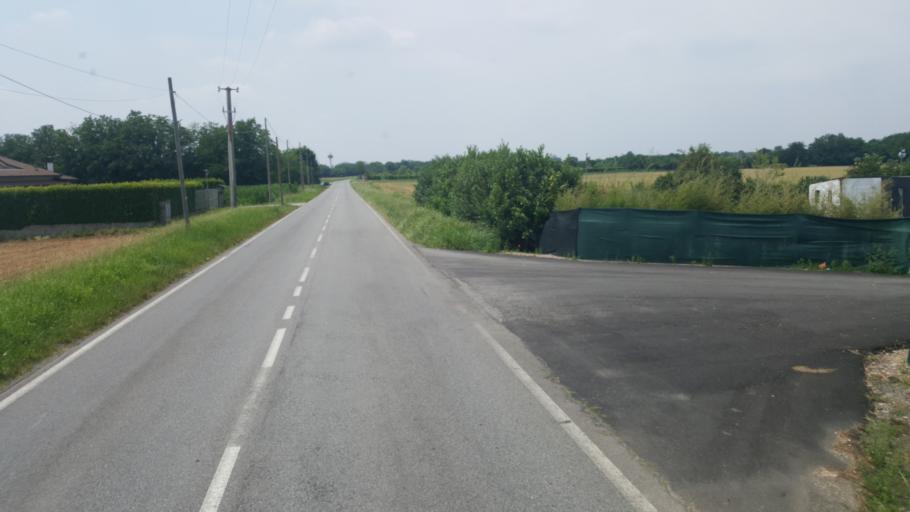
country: IT
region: Lombardy
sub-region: Provincia di Monza e Brianza
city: Cavenago di Brianza
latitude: 45.5952
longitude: 9.4055
